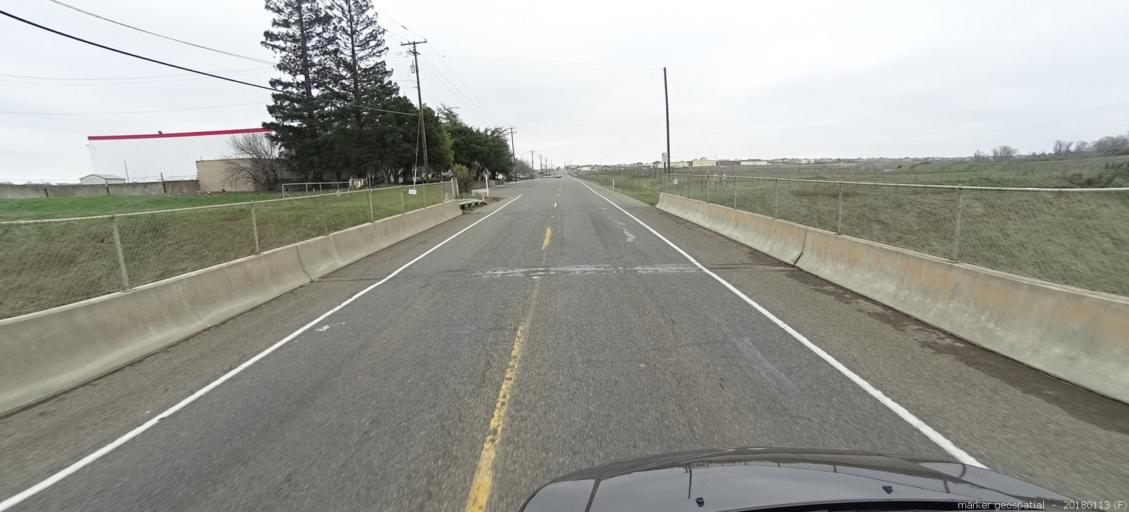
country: US
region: California
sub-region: Sacramento County
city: Rancho Cordova
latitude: 38.5594
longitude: -121.2540
